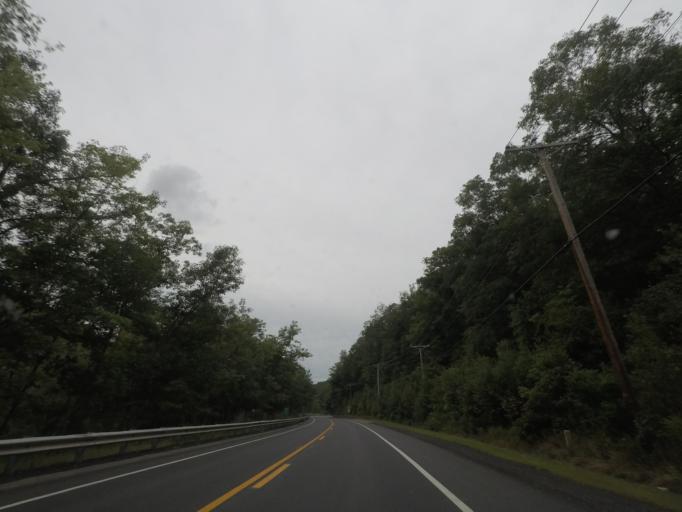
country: US
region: Massachusetts
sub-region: Hampshire County
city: Ware
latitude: 42.2050
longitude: -72.2620
